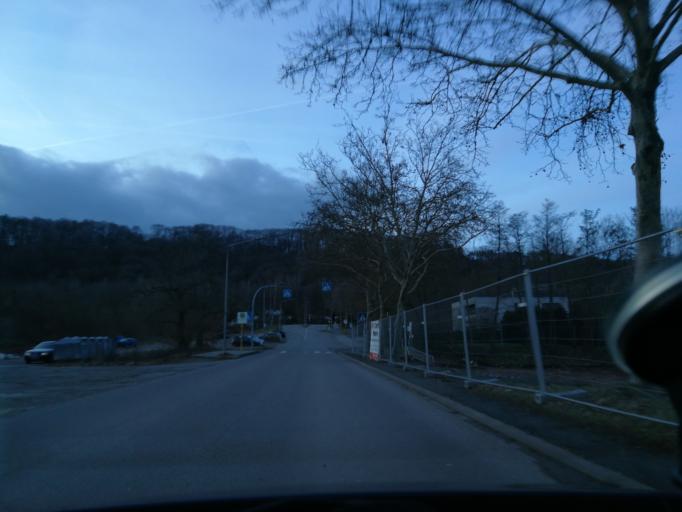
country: DE
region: Rheinland-Pfalz
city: Kenn
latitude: 49.7861
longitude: 6.6780
